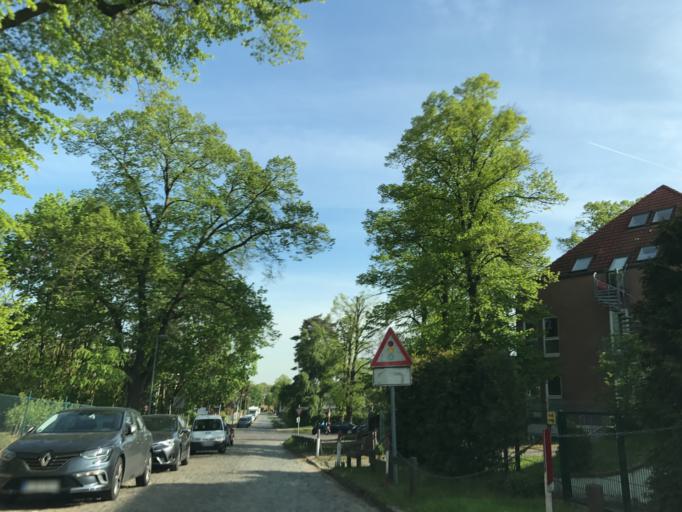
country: DE
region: Berlin
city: Staaken
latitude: 52.5256
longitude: 13.1331
